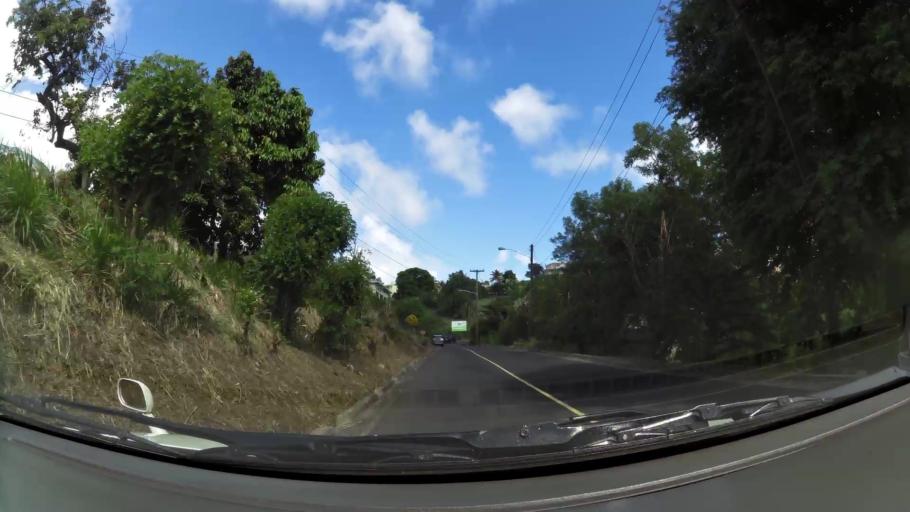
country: VC
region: Saint George
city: Kingstown
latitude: 13.1311
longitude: -61.1885
